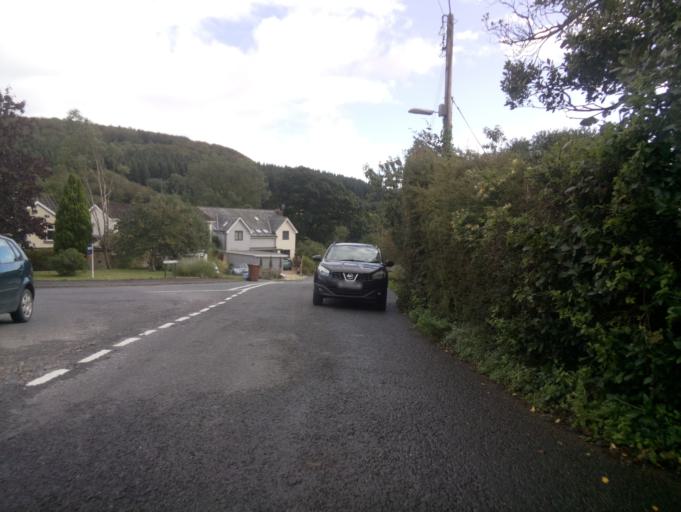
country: GB
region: England
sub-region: Devon
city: Ivybridge
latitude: 50.3606
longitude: -3.9171
